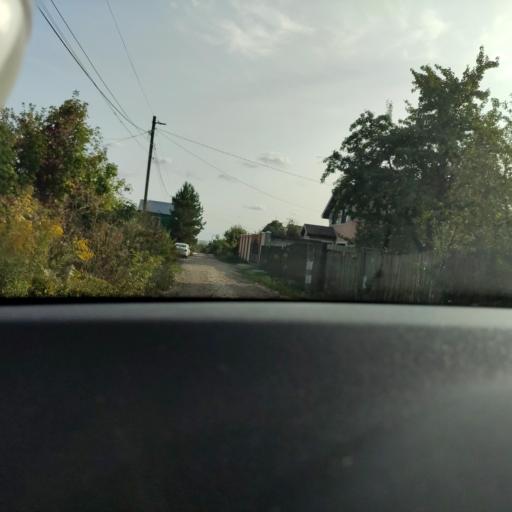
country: RU
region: Samara
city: Petra-Dubrava
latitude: 53.2839
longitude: 50.2951
